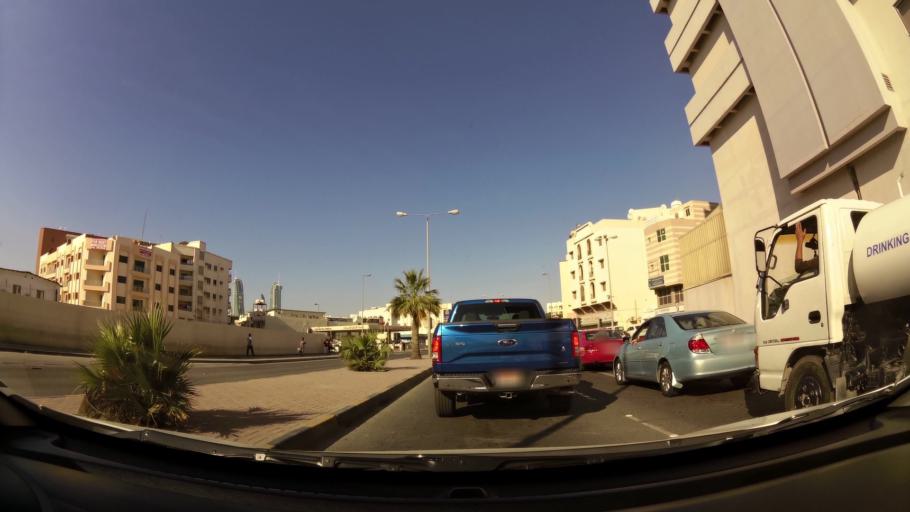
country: BH
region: Manama
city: Manama
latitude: 26.2231
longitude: 50.5706
